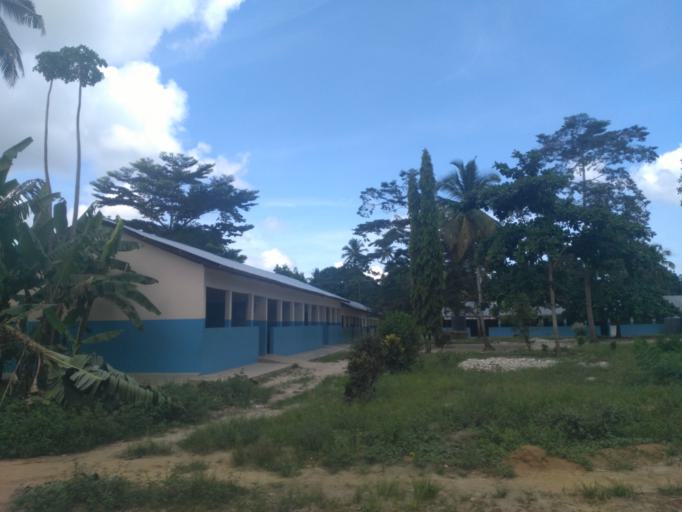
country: TZ
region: Zanzibar North
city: Gamba
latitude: -5.9766
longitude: 39.2957
